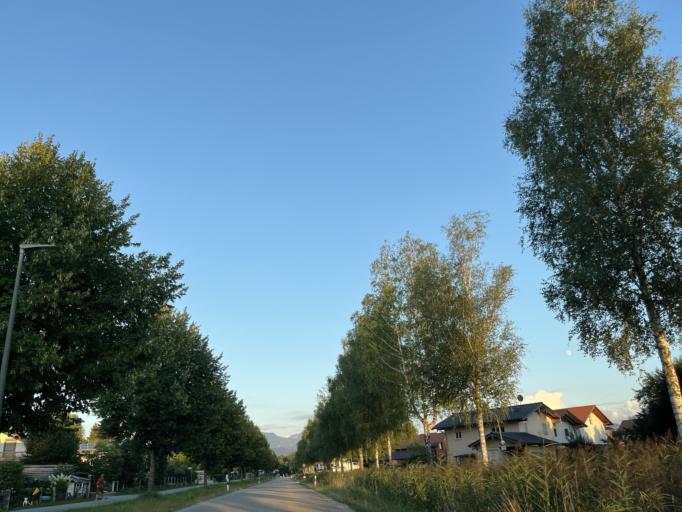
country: DE
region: Bavaria
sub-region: Upper Bavaria
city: Raubling
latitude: 47.7909
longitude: 12.0756
